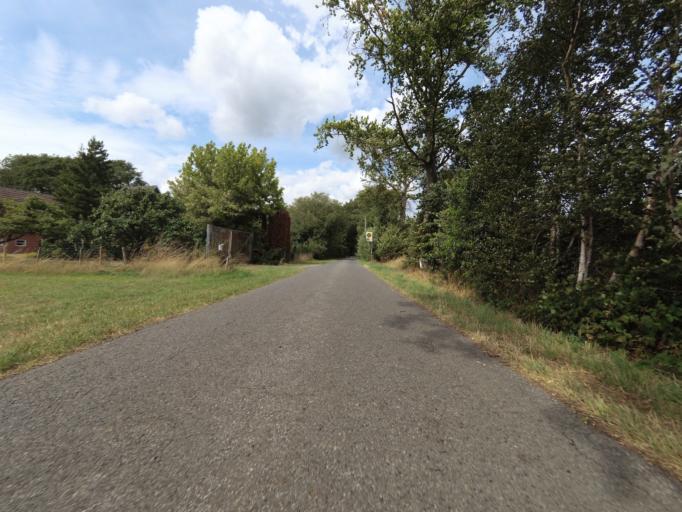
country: DE
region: North Rhine-Westphalia
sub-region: Regierungsbezirk Munster
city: Ahaus
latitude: 52.1439
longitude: 6.9924
